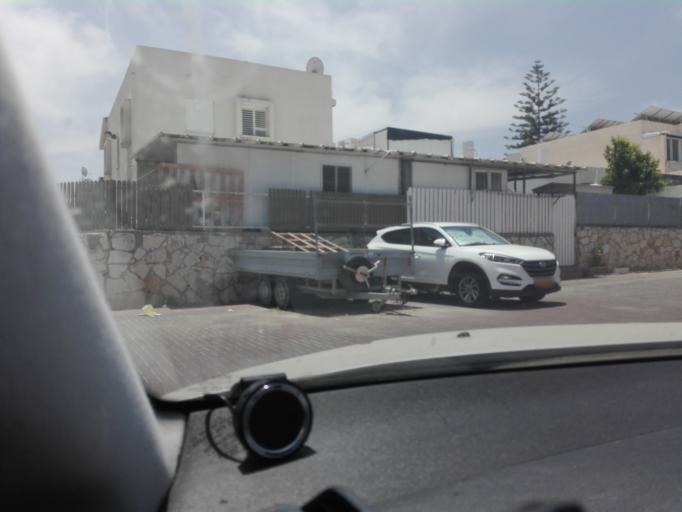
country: IL
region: Central District
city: Bene 'Ayish
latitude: 31.7355
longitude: 34.7422
